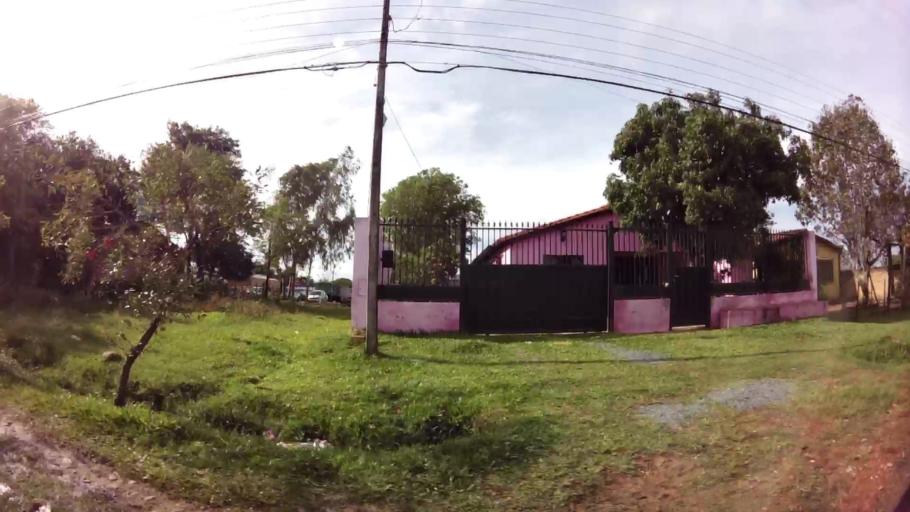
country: PY
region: Central
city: Limpio
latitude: -25.1712
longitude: -57.4907
